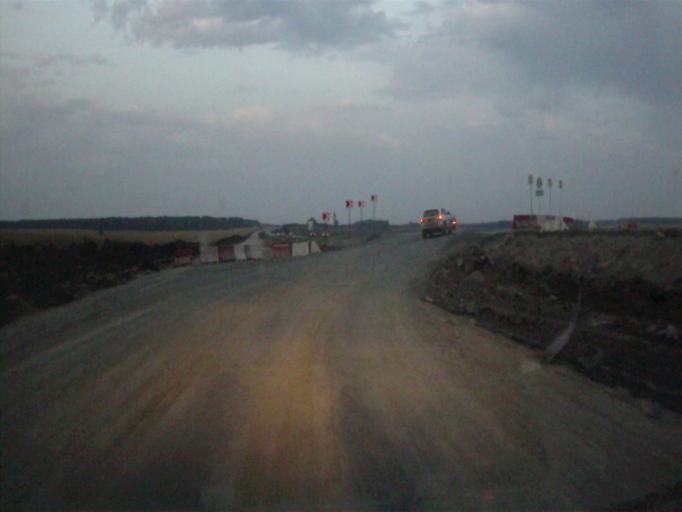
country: RU
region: Chelyabinsk
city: Timiryazevskiy
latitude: 55.2075
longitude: 60.8080
